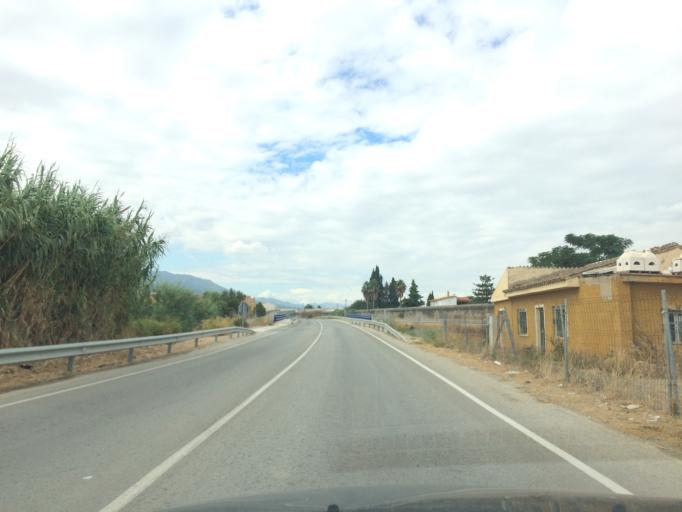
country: ES
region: Andalusia
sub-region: Provincia de Malaga
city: Alhaurin de la Torre
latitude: 36.6874
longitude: -4.5257
